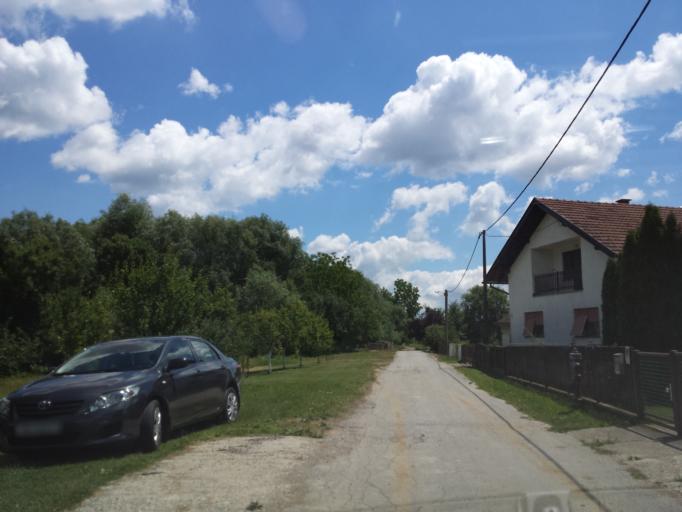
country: HR
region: Sisacko-Moslavacka
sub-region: Grad Sisak
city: Sisak
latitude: 45.5185
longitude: 16.3959
